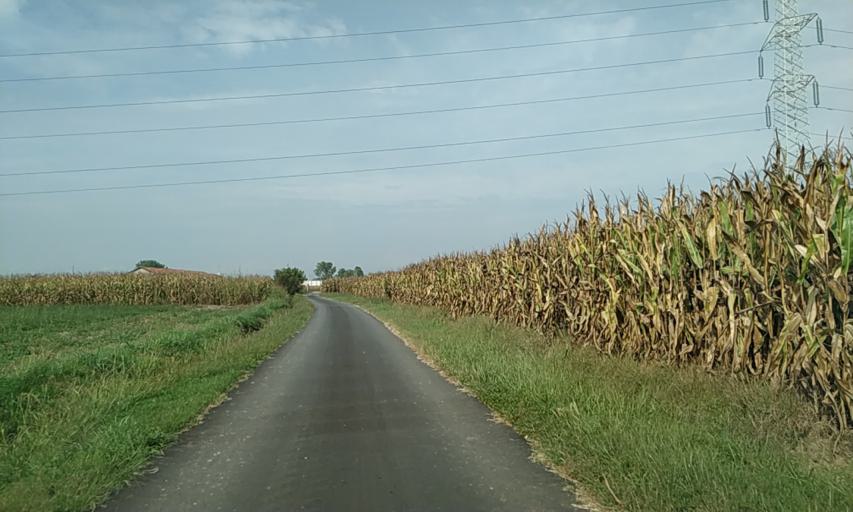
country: IT
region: Piedmont
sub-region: Provincia di Vercelli
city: Livorno Ferraris
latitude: 45.3130
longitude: 8.0712
